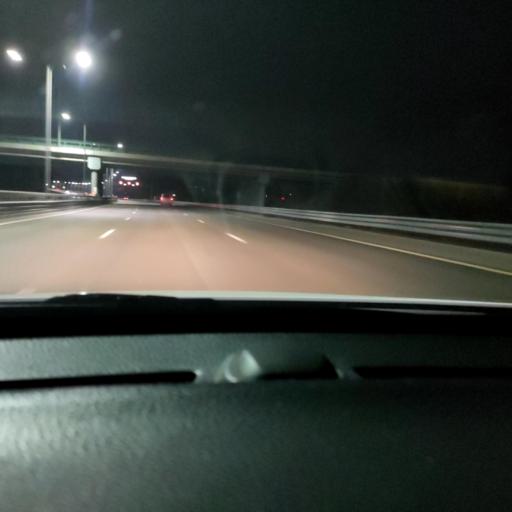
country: RU
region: Voronezj
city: Somovo
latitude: 51.7259
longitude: 39.3112
